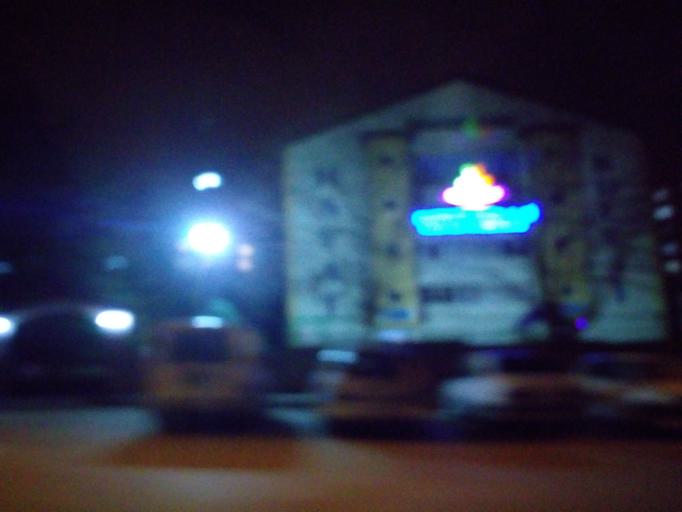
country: TR
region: Ankara
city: Ankara
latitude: 39.9795
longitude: 32.8253
